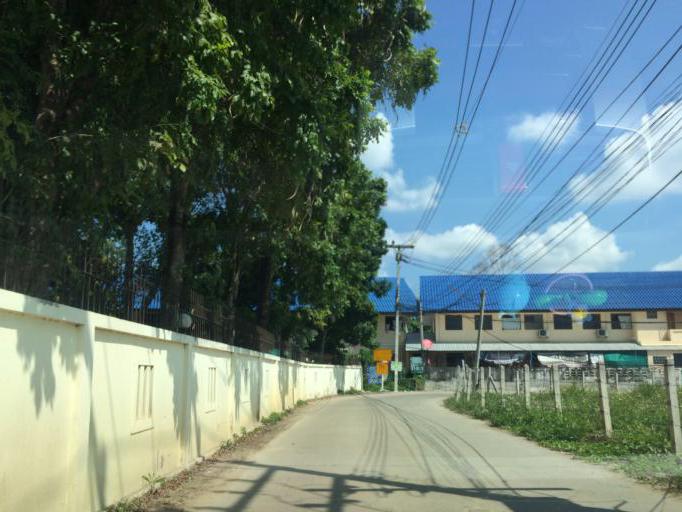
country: TH
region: Chiang Mai
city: Saraphi
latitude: 18.7461
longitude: 99.0222
